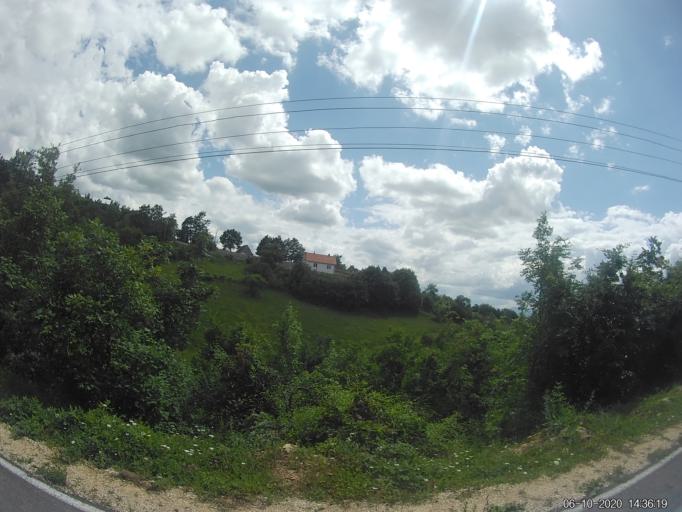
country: XK
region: Prizren
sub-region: Komuna e Therandes
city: Budakovo
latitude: 42.4109
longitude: 20.9370
